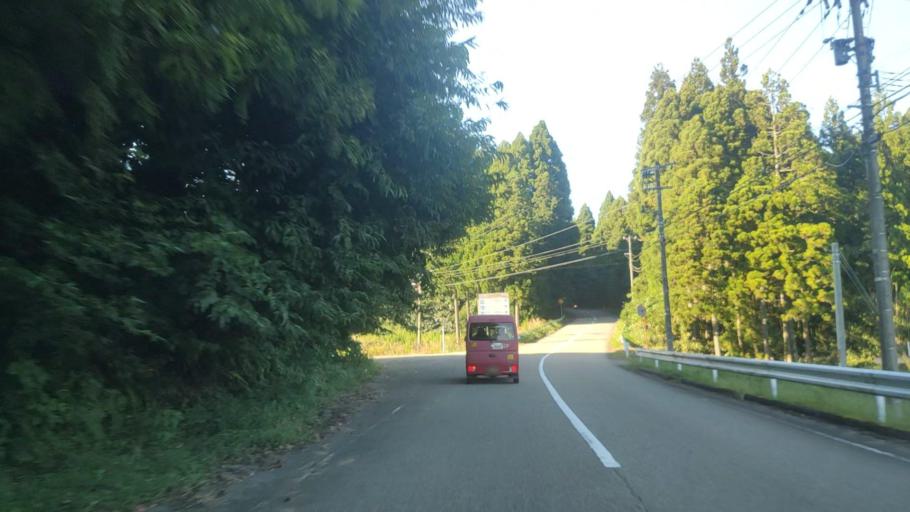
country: JP
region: Ishikawa
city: Nanao
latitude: 37.1090
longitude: 136.9618
